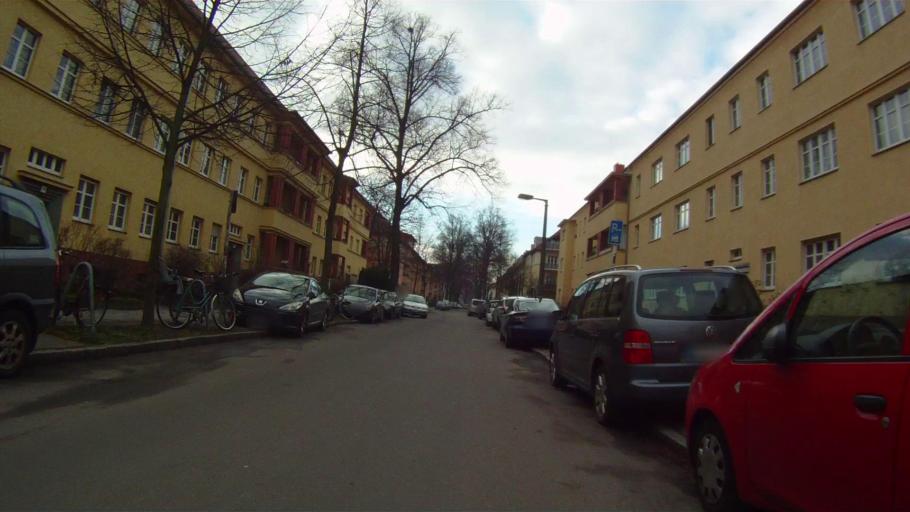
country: DE
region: Berlin
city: Karlshorst
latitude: 52.4915
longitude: 13.5250
